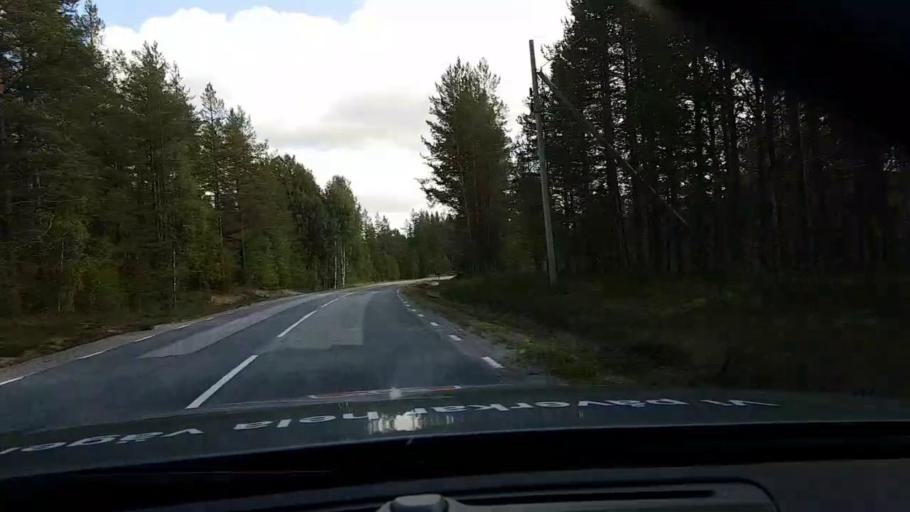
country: SE
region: Vaesterbotten
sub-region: Asele Kommun
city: Asele
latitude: 63.7920
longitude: 17.5816
